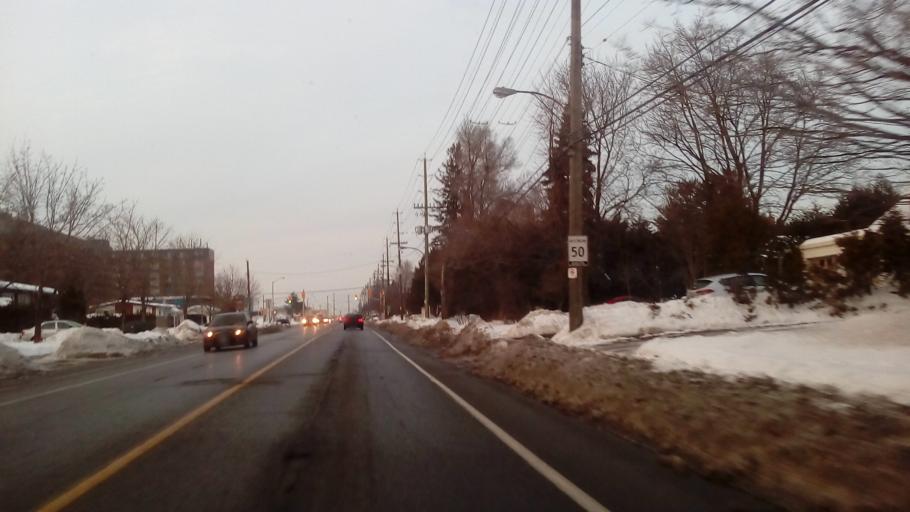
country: CA
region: Ontario
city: Ottawa
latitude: 45.3943
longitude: -75.6204
